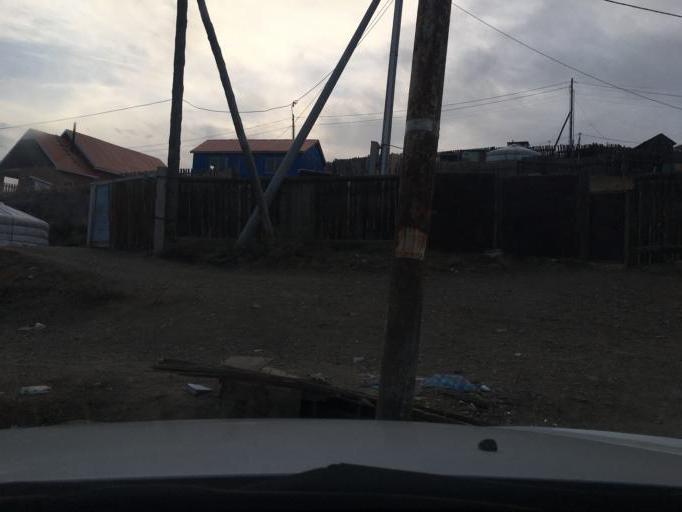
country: MN
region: Ulaanbaatar
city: Ulaanbaatar
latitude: 47.9331
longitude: 106.8578
